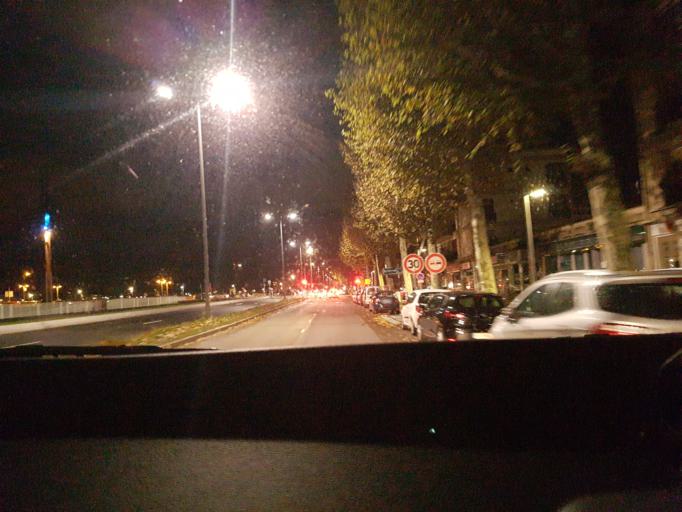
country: FR
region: Haute-Normandie
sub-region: Departement de la Seine-Maritime
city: Rouen
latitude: 49.4373
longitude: 1.0858
